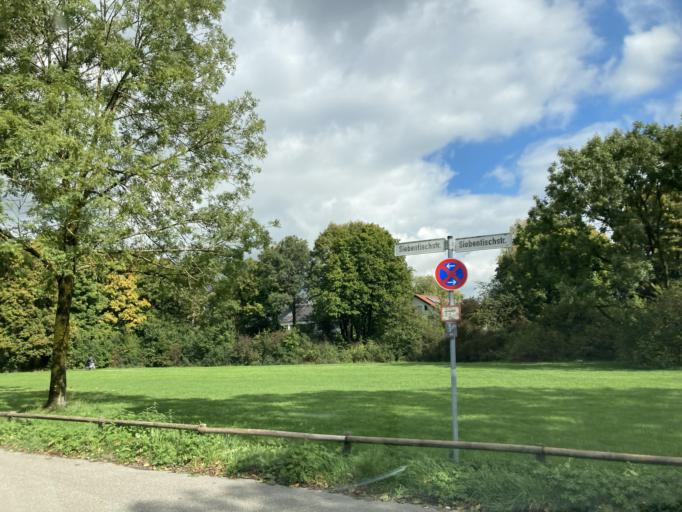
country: DE
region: Bavaria
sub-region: Swabia
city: Augsburg
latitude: 48.3498
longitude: 10.9179
